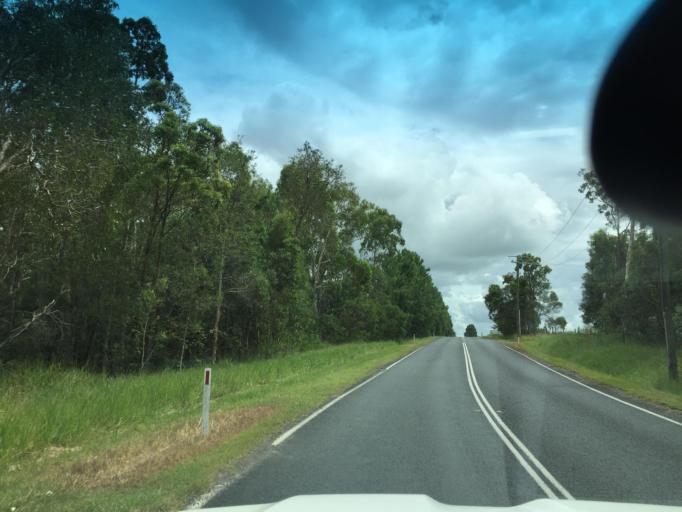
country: AU
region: Queensland
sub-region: Moreton Bay
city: Morayfield
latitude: -27.1193
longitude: 152.9790
